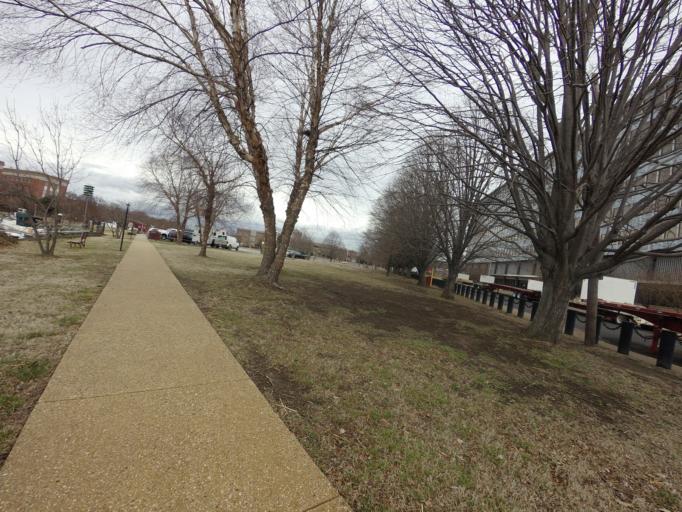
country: US
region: Washington, D.C.
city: Washington, D.C.
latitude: 38.8636
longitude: -77.0138
